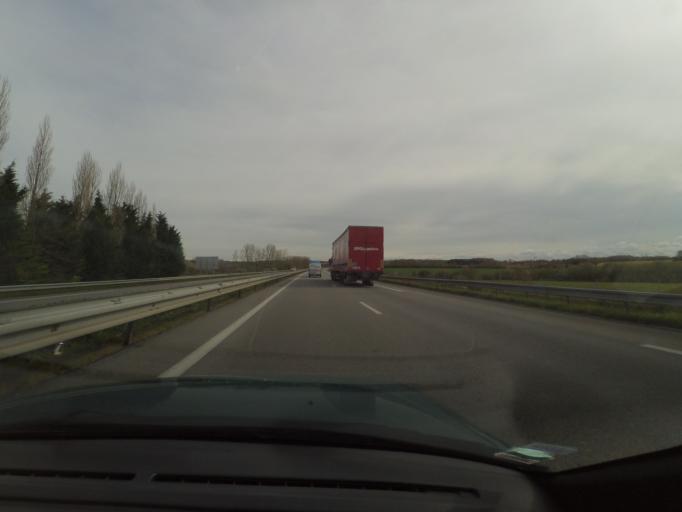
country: FR
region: Pays de la Loire
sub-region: Departement de la Loire-Atlantique
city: Mauves-sur-Loire
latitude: 47.3307
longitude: -1.3998
